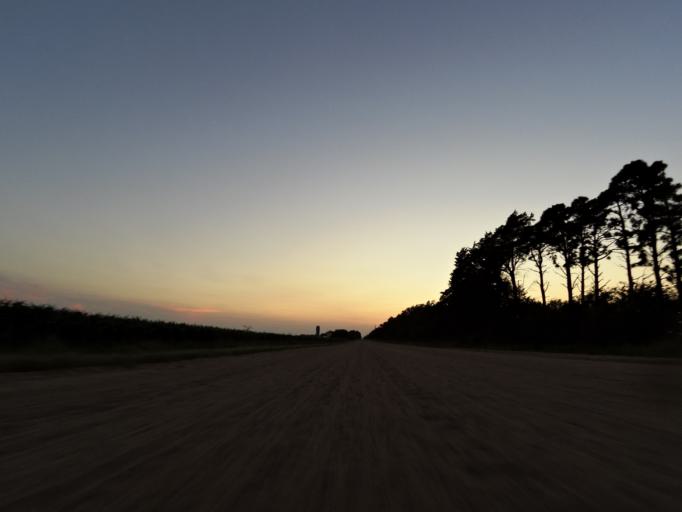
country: US
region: Kansas
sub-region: Reno County
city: South Hutchinson
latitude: 37.9991
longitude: -98.0339
